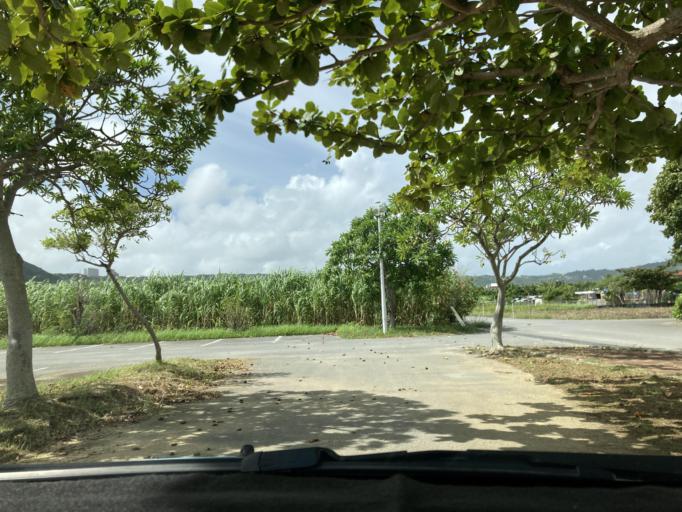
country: JP
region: Okinawa
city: Ginowan
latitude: 26.1697
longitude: 127.7875
